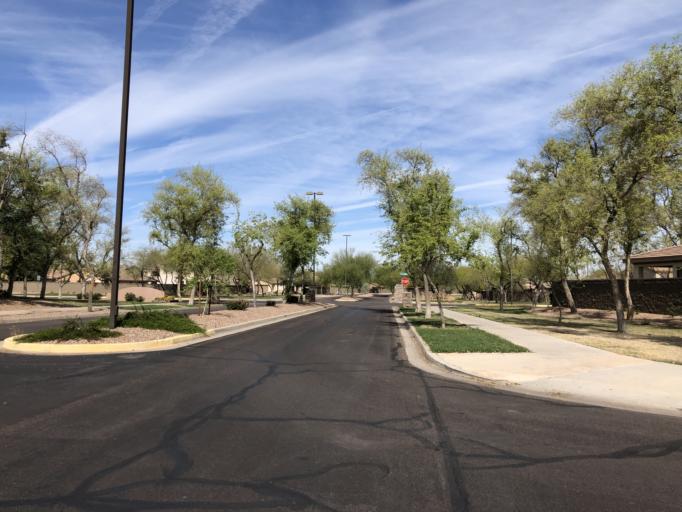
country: US
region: Arizona
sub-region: Maricopa County
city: Queen Creek
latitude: 33.2675
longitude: -111.7004
